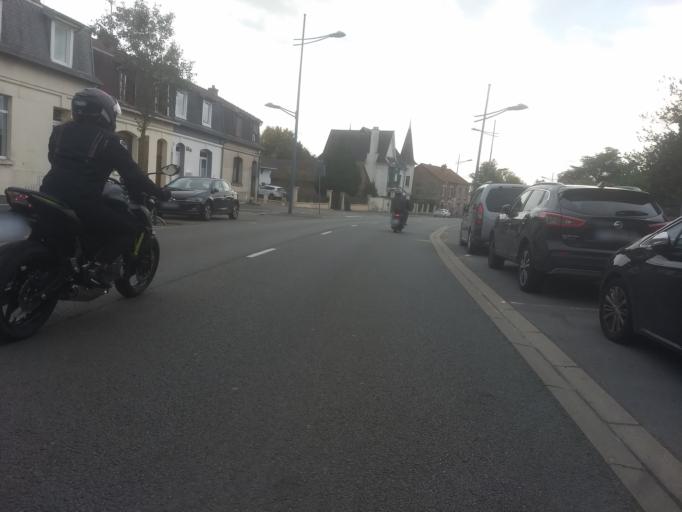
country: FR
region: Nord-Pas-de-Calais
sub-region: Departement du Pas-de-Calais
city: Beaurains
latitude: 50.2667
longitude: 2.7850
